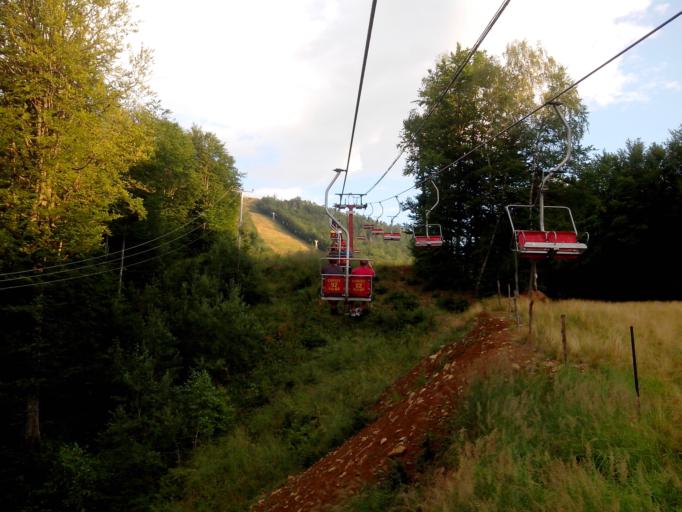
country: RO
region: Maramures
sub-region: Comuna Sisesti
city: Surdesti
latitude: 47.6679
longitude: 23.7819
